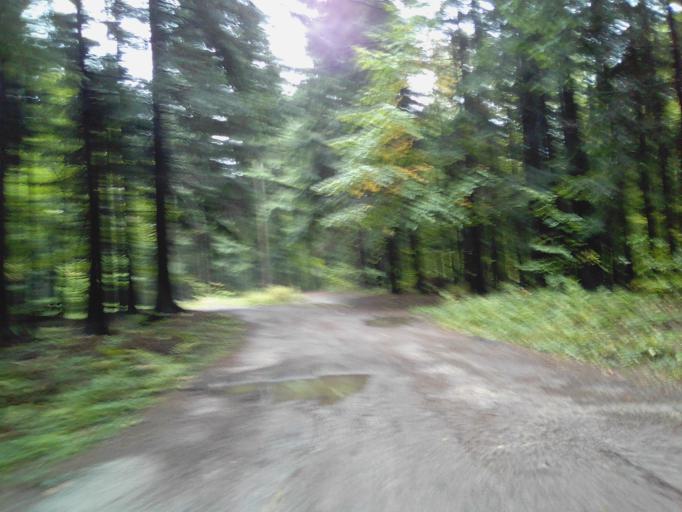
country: PL
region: Subcarpathian Voivodeship
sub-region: Powiat strzyzowski
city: Gwoznica Gorna
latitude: 49.8409
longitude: 22.0208
